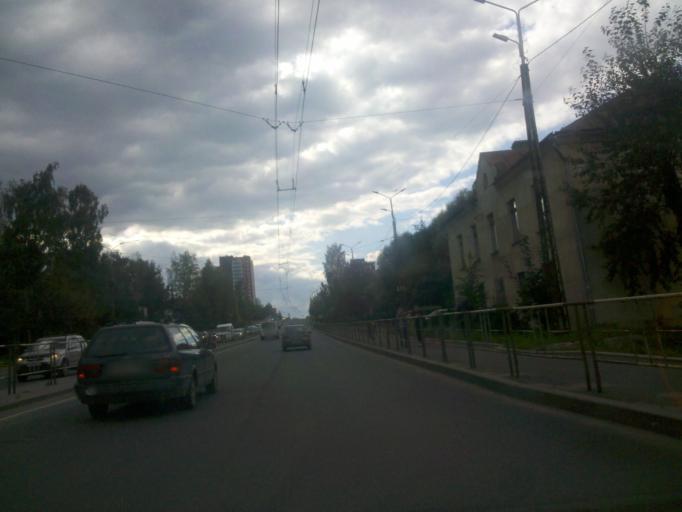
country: RU
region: Republic of Karelia
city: Petrozavodsk
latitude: 61.7875
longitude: 34.3371
